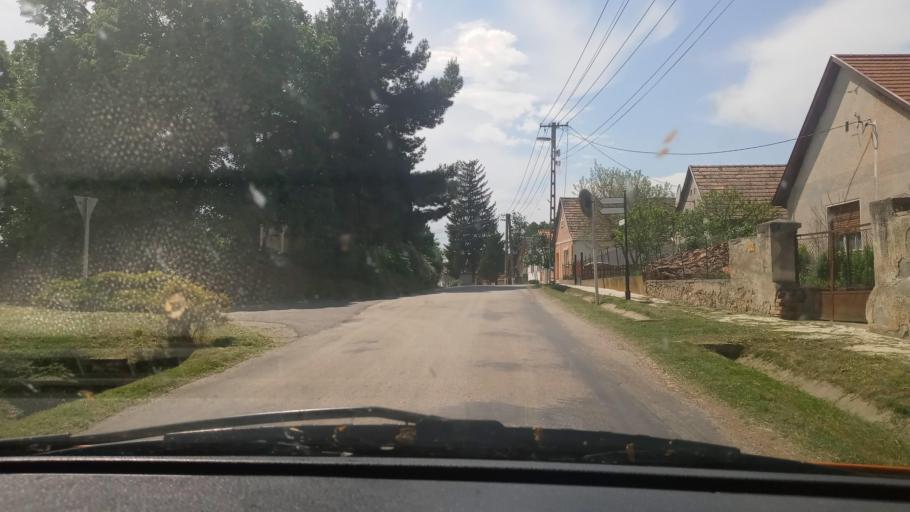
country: HU
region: Baranya
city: Beremend
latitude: 45.8223
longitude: 18.3856
